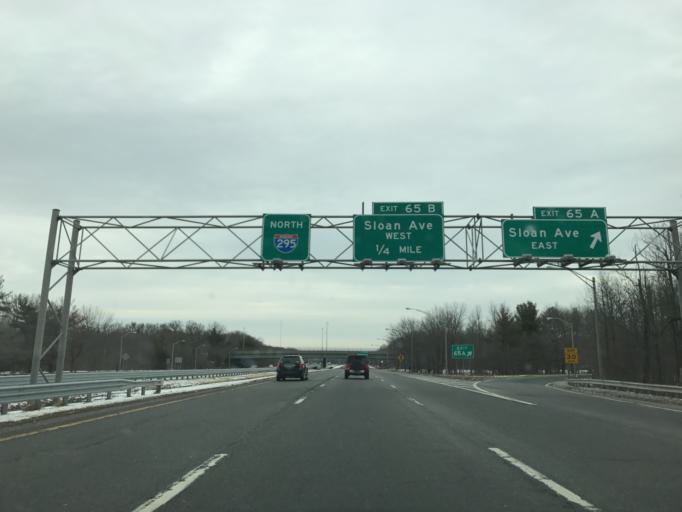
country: US
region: New Jersey
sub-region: Mercer County
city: Mercerville
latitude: 40.2490
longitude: -74.6980
